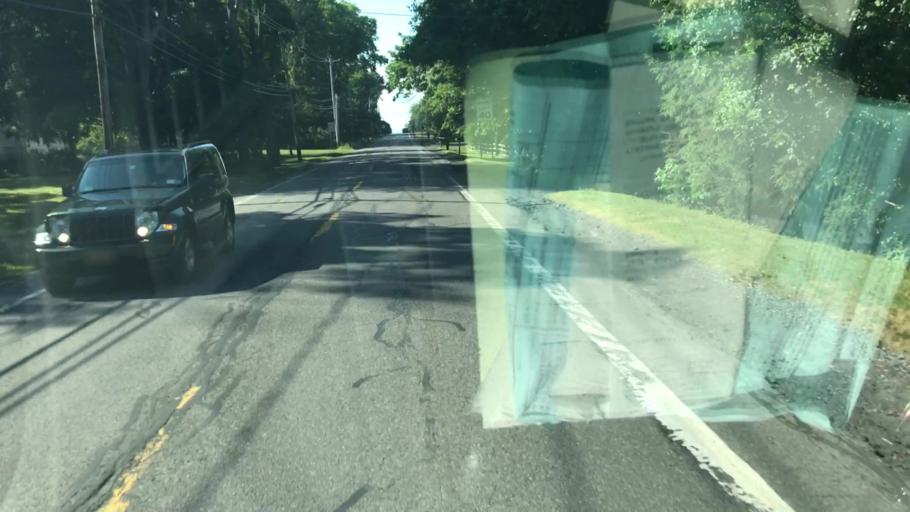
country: US
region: New York
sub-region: Onondaga County
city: Skaneateles
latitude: 42.9364
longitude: -76.4104
